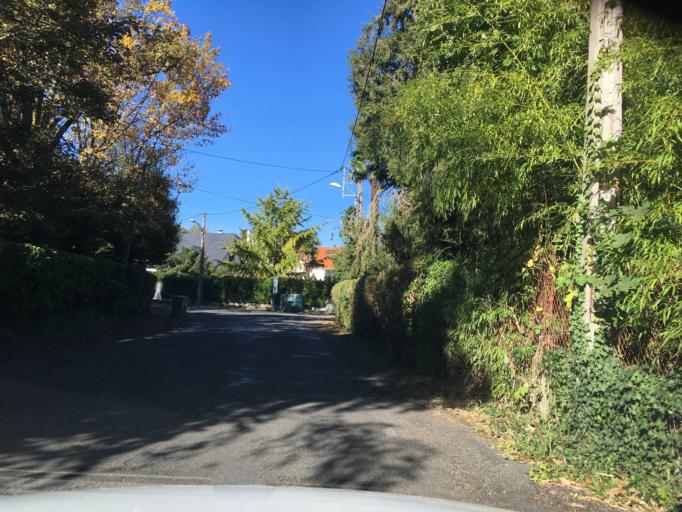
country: FR
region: Aquitaine
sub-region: Departement des Pyrenees-Atlantiques
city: Bizanos
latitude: 43.3026
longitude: -0.3461
